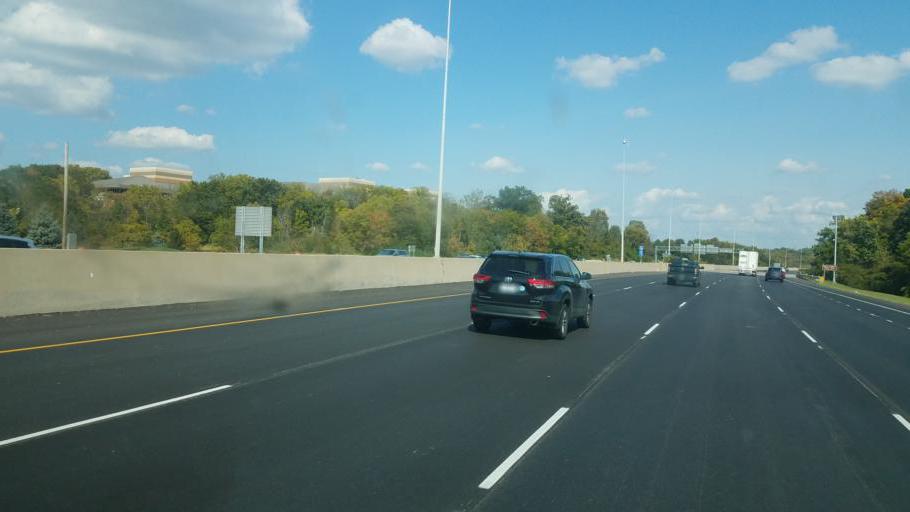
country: US
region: Ohio
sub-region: Franklin County
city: Dublin
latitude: 40.1066
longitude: -83.1230
